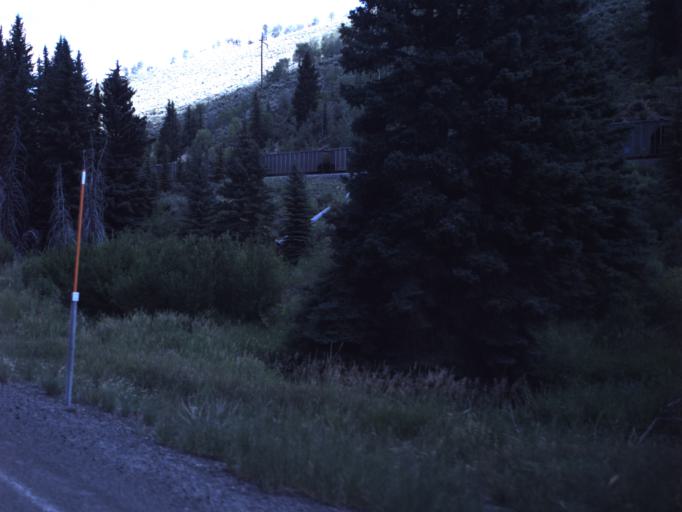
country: US
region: Utah
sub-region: Sanpete County
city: Fairview
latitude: 39.6888
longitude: -111.1544
